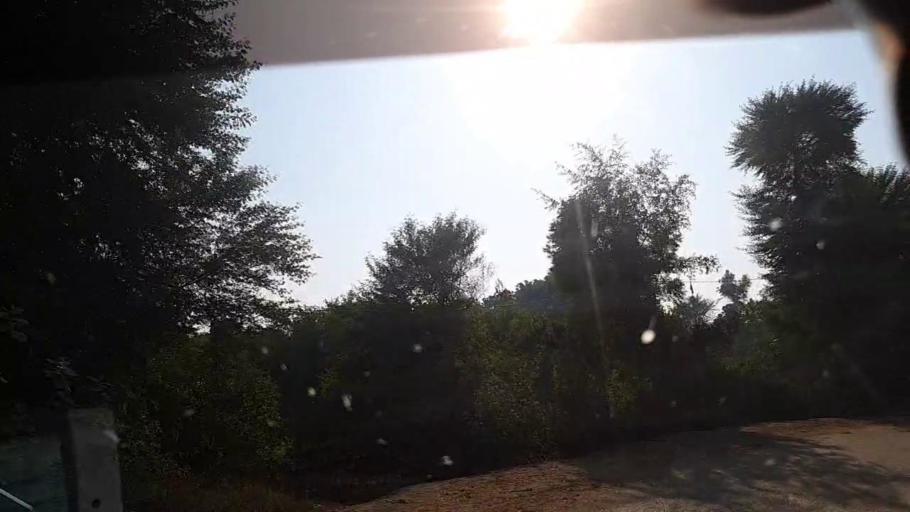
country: PK
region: Sindh
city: Hingorja
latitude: 27.2216
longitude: 68.2703
